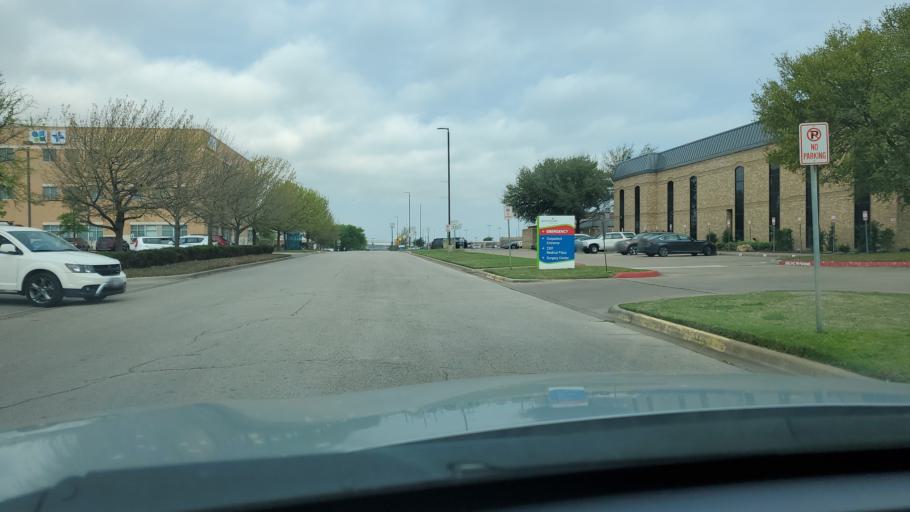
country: US
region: Texas
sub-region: Bell County
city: Fort Hood
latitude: 31.1118
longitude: -97.8005
